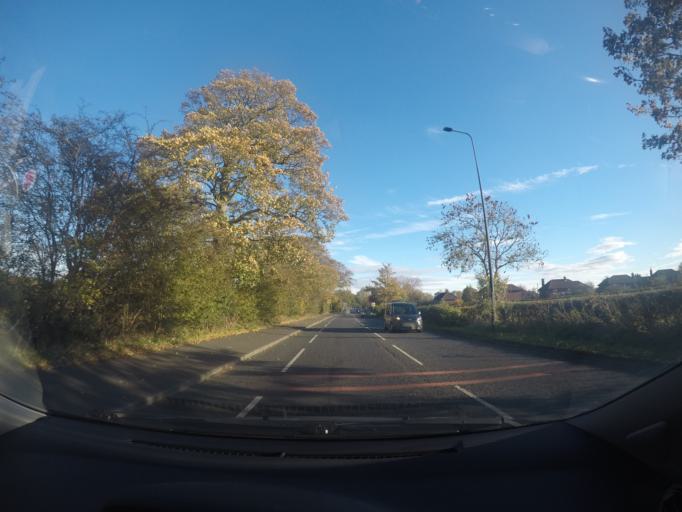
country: GB
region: England
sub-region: City of York
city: Nether Poppleton
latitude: 53.9712
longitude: -1.1368
